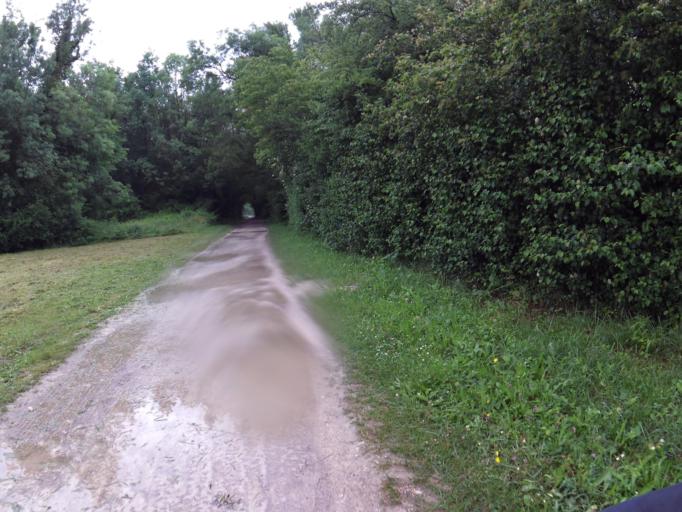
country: FR
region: Poitou-Charentes
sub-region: Departement de la Charente
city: Gond-Pontouvre
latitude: 45.6735
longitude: 0.1538
